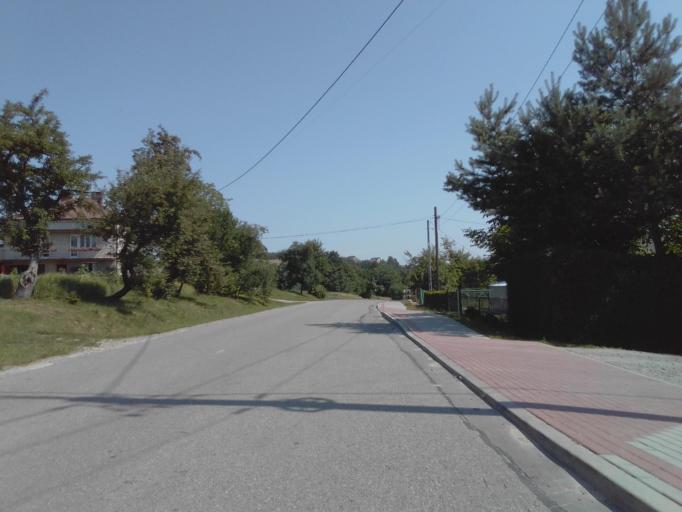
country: PL
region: Subcarpathian Voivodeship
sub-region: Powiat ropczycko-sedziszowski
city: Ropczyce
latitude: 50.0263
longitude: 21.6367
